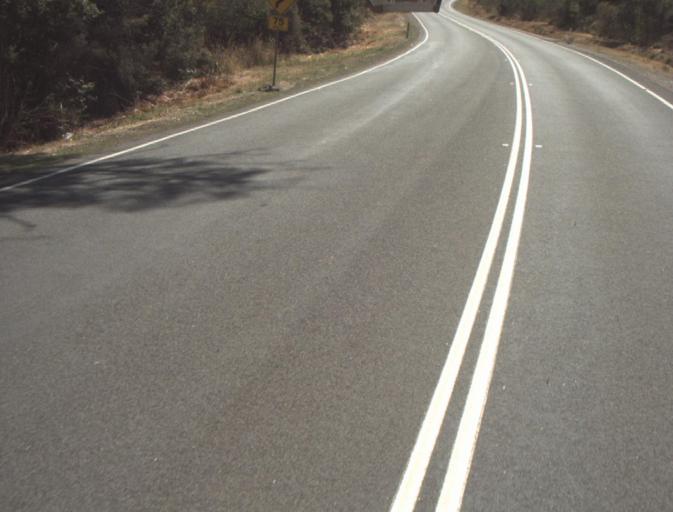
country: AU
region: Tasmania
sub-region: Launceston
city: Mayfield
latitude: -41.3590
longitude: 147.1430
